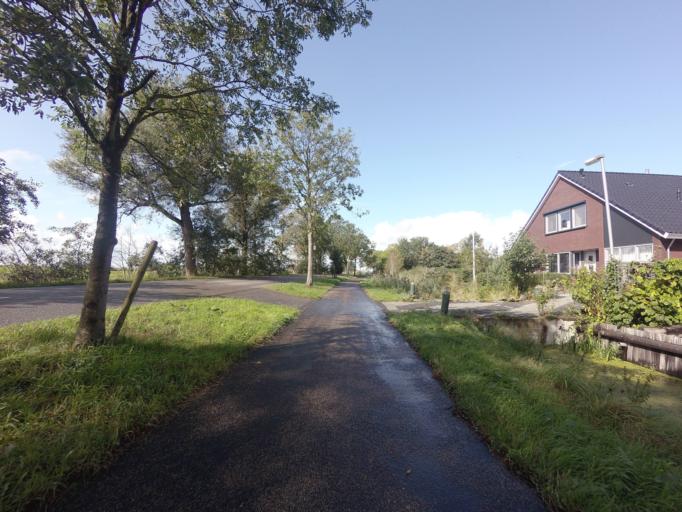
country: NL
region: Friesland
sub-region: Gemeente Boarnsterhim
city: Warten
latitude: 53.1498
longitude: 5.8808
